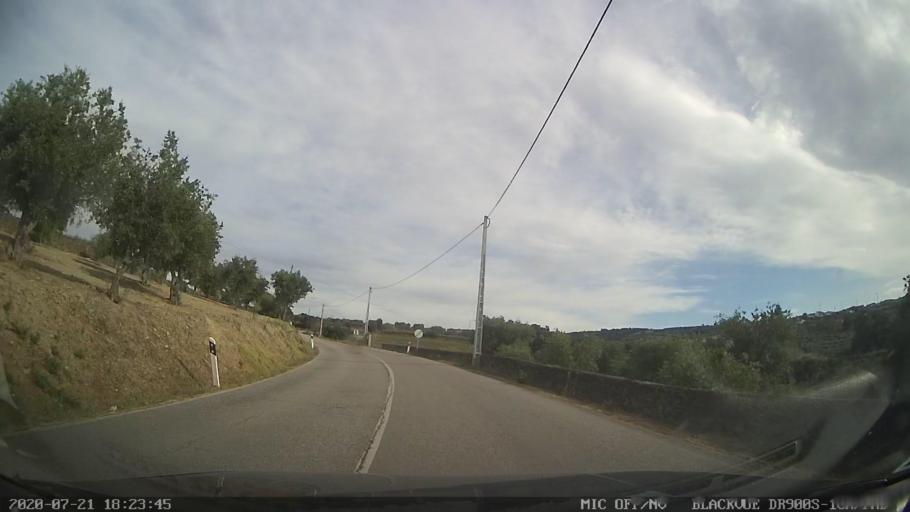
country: PT
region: Viseu
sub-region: Sao Joao da Pesqueira
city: Sao Joao da Pesqueira
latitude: 41.0747
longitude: -7.3917
